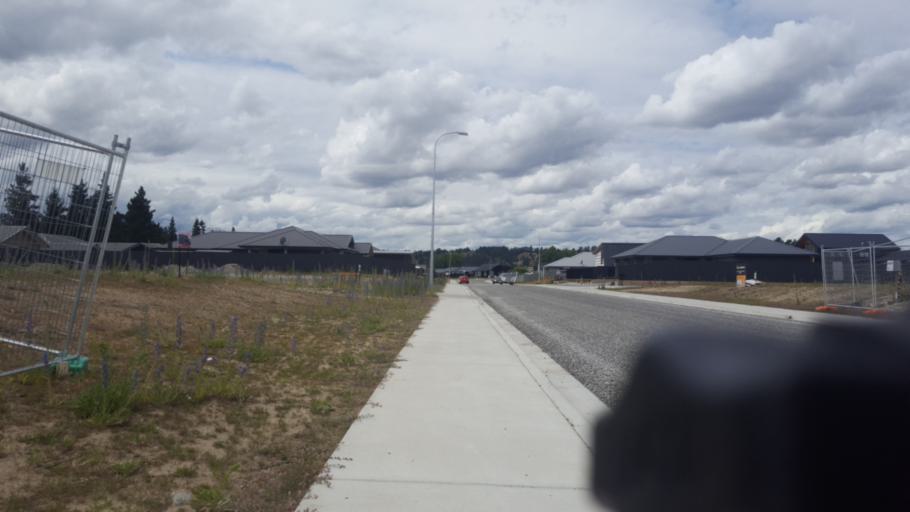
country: NZ
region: Otago
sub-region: Queenstown-Lakes District
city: Wanaka
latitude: -45.2446
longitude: 169.3729
